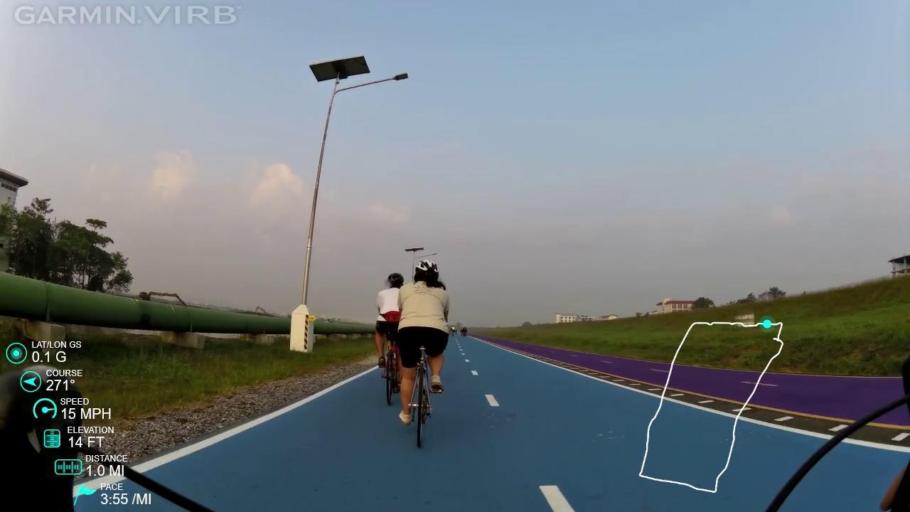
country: TH
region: Bangkok
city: Lat Krabang
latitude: 13.7081
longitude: 100.7817
